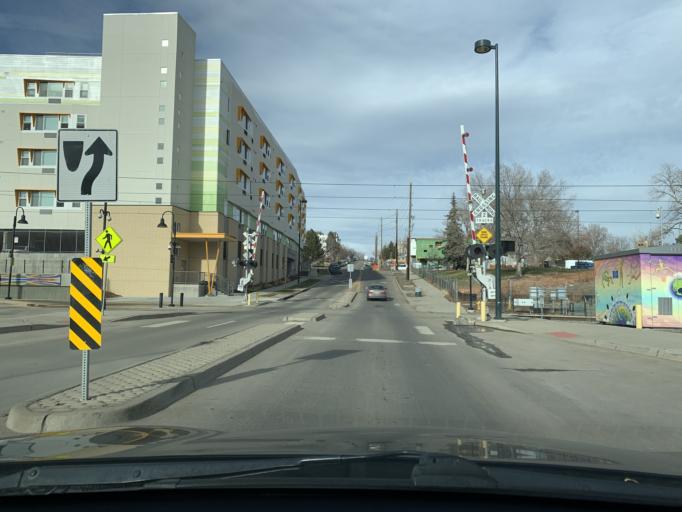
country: US
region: Colorado
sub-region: Jefferson County
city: Edgewater
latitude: 39.7354
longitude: -105.0321
